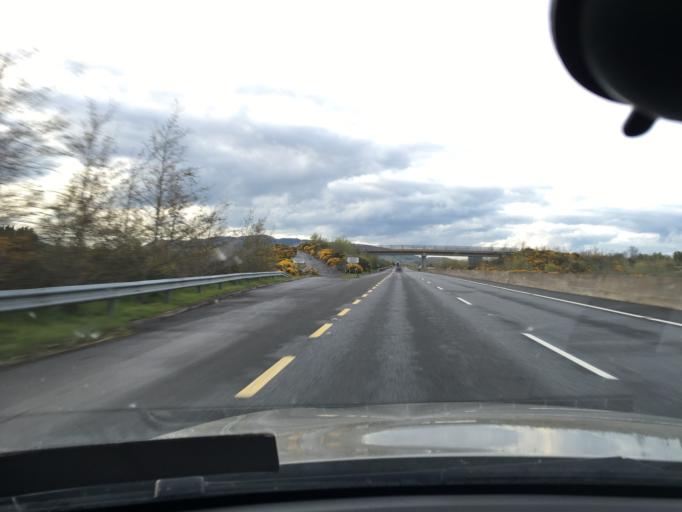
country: GB
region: Northern Ireland
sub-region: Newry and Mourne District
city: Newry
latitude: 54.1061
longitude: -6.3650
